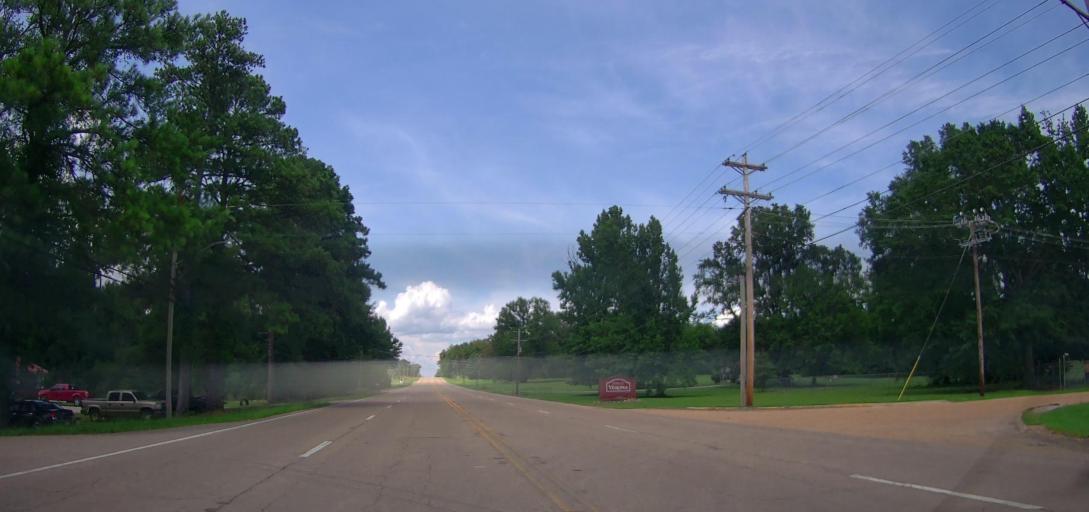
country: US
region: Mississippi
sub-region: Lee County
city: Verona
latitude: 34.1697
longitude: -88.7196
